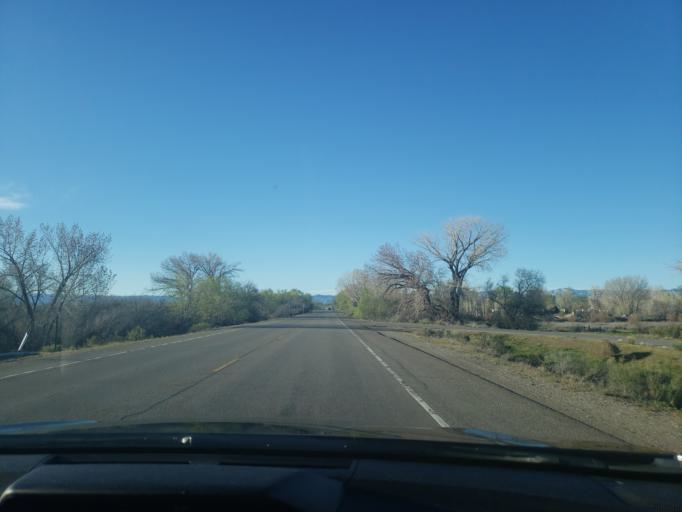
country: US
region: Colorado
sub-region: Mesa County
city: Fruita
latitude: 39.1427
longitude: -108.7382
